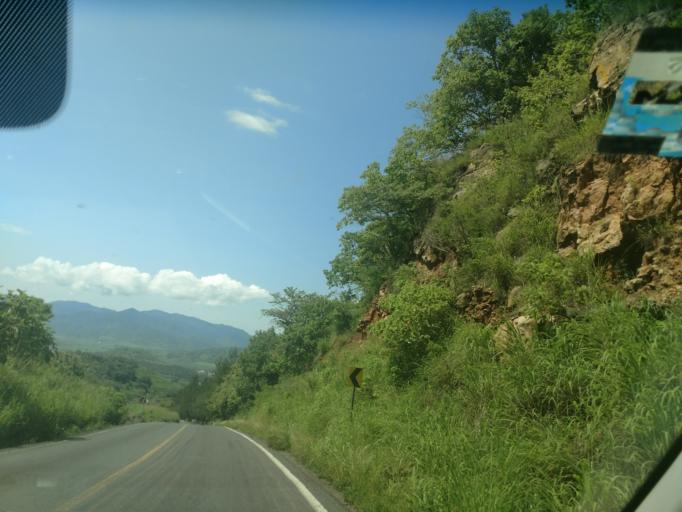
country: MX
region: Jalisco
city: Talpa de Allende
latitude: 20.4115
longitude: -104.8081
